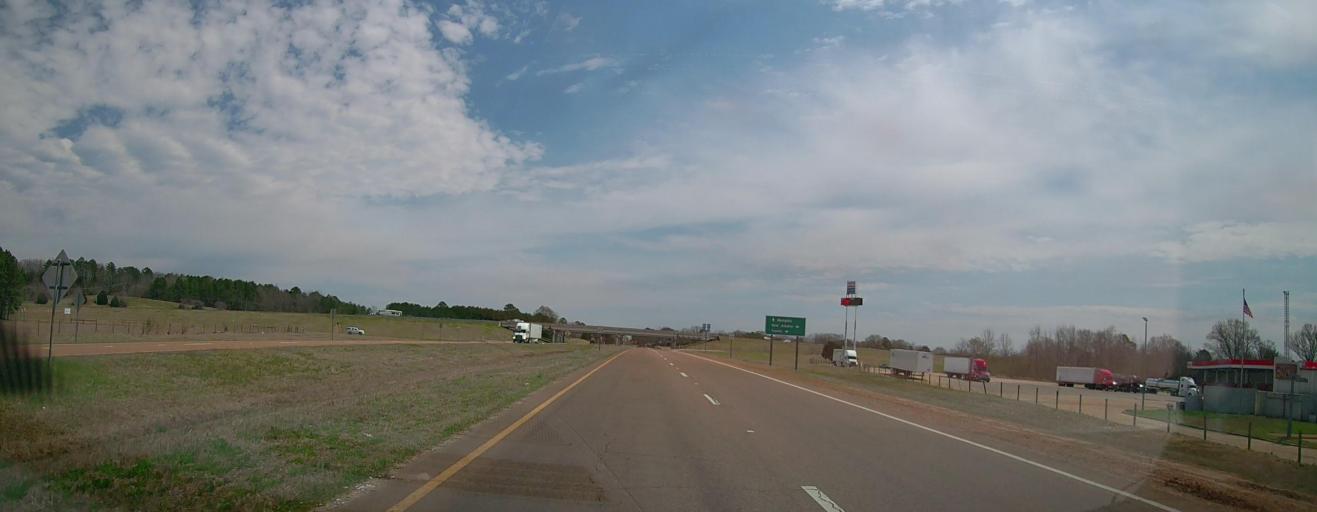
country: US
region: Mississippi
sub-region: Benton County
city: Ashland
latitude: 34.6184
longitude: -89.2059
